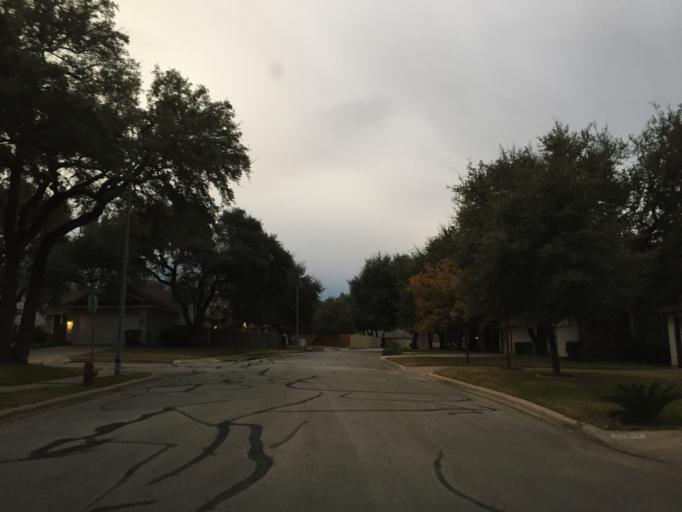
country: US
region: Texas
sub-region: Williamson County
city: Jollyville
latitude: 30.4490
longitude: -97.7525
